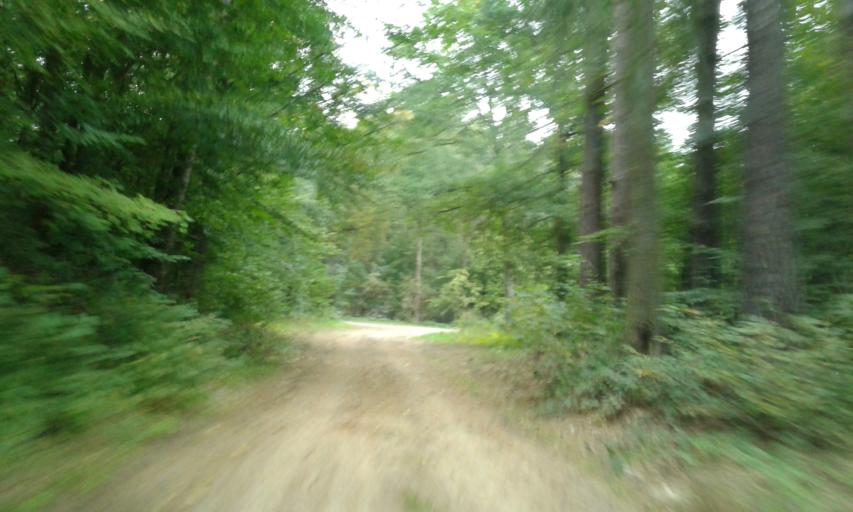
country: PL
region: West Pomeranian Voivodeship
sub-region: Powiat choszczenski
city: Pelczyce
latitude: 53.0832
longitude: 15.2666
